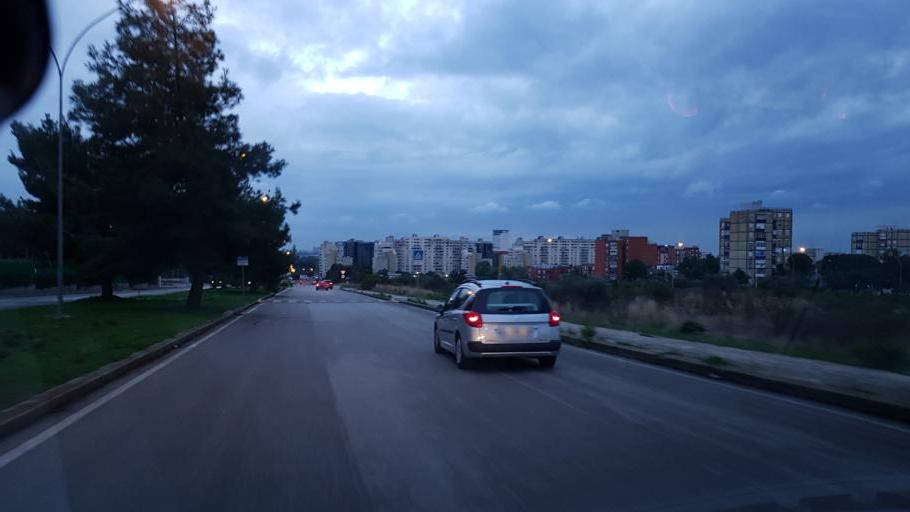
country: IT
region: Apulia
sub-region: Provincia di Taranto
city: Paolo VI
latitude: 40.5250
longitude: 17.2812
